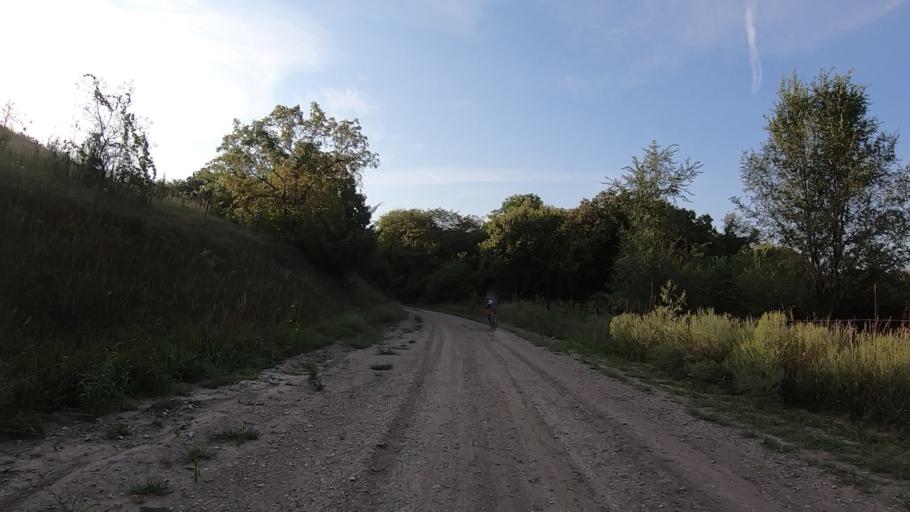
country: US
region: Kansas
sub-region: Marshall County
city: Blue Rapids
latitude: 39.7461
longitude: -96.7527
